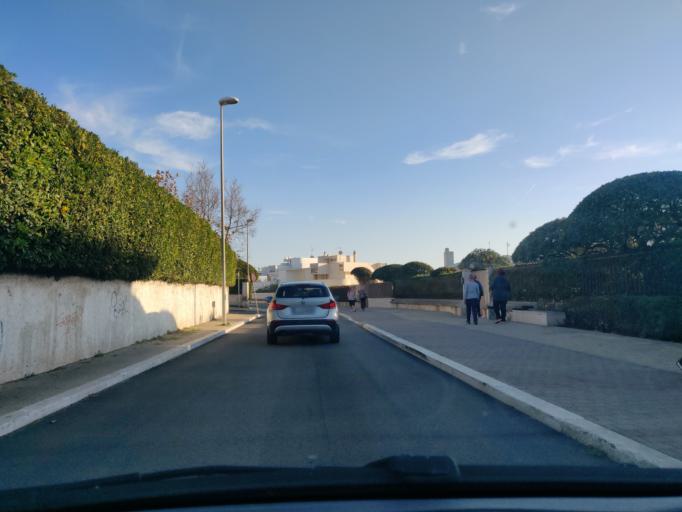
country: IT
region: Latium
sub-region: Citta metropolitana di Roma Capitale
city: Santa Marinella
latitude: 42.0307
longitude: 11.8349
